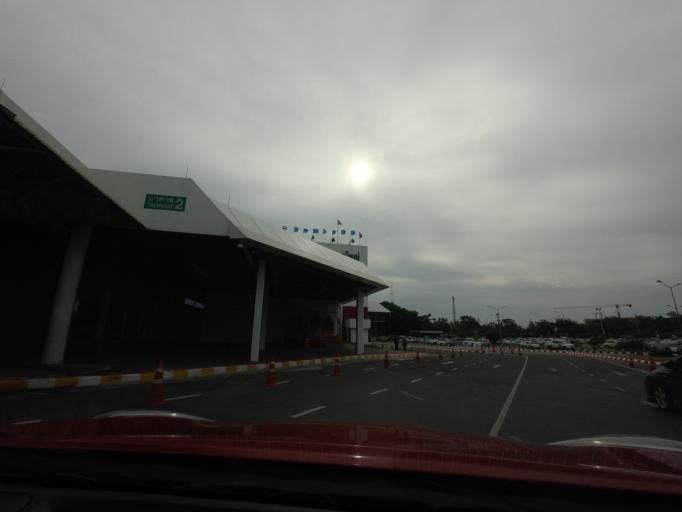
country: TH
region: Songkhla
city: Khlong Hoi Khong
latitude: 6.9368
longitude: 100.3941
